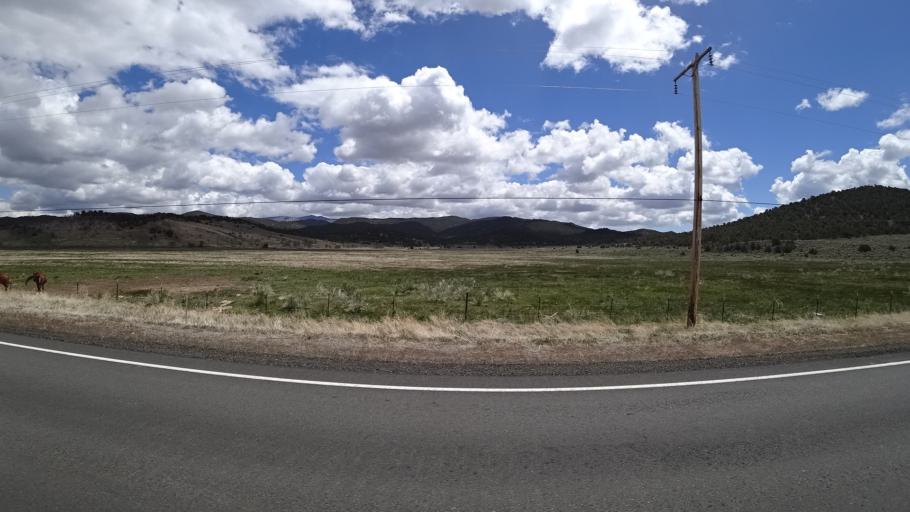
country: US
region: California
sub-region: Mono County
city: Bridgeport
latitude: 38.2175
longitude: -119.2301
